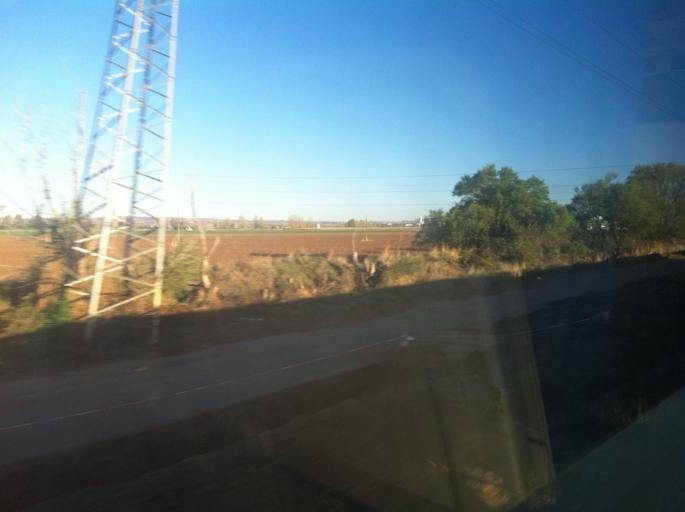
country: ES
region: Castille and Leon
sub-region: Provincia de Valladolid
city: Cabezon
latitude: 41.7420
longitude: -4.6473
